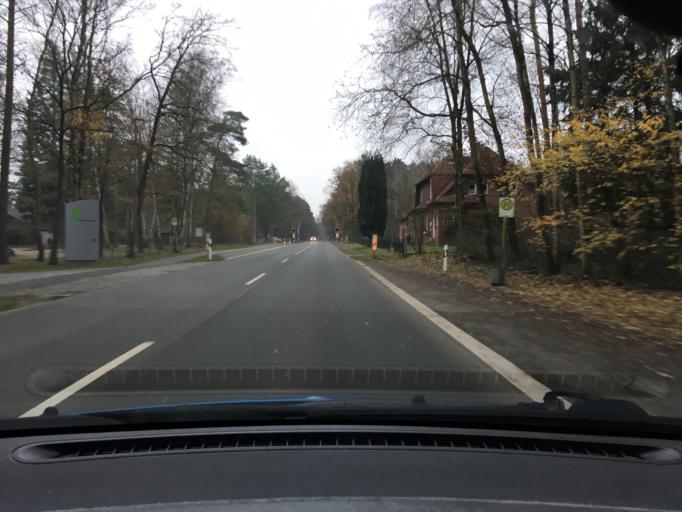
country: DE
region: Lower Saxony
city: Soltau
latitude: 53.0000
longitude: 9.8596
